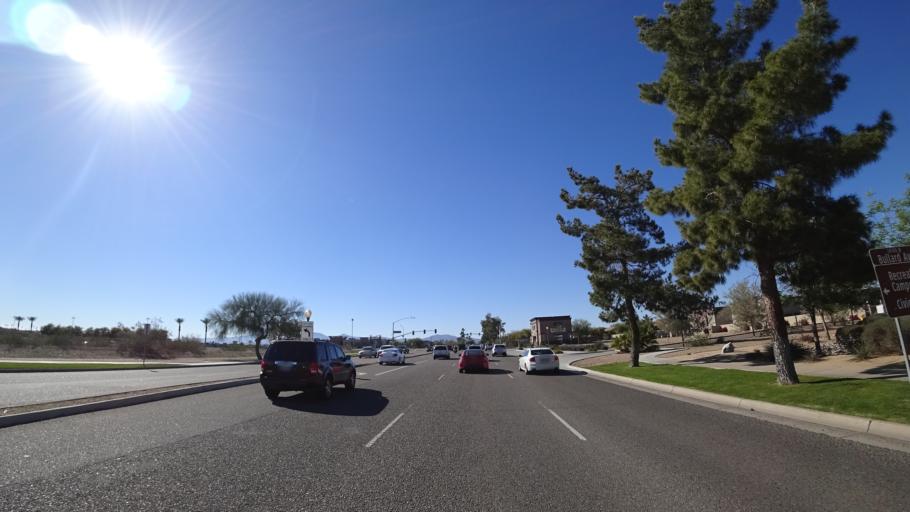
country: US
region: Arizona
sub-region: Maricopa County
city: Sun City West
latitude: 33.6387
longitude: -112.3752
